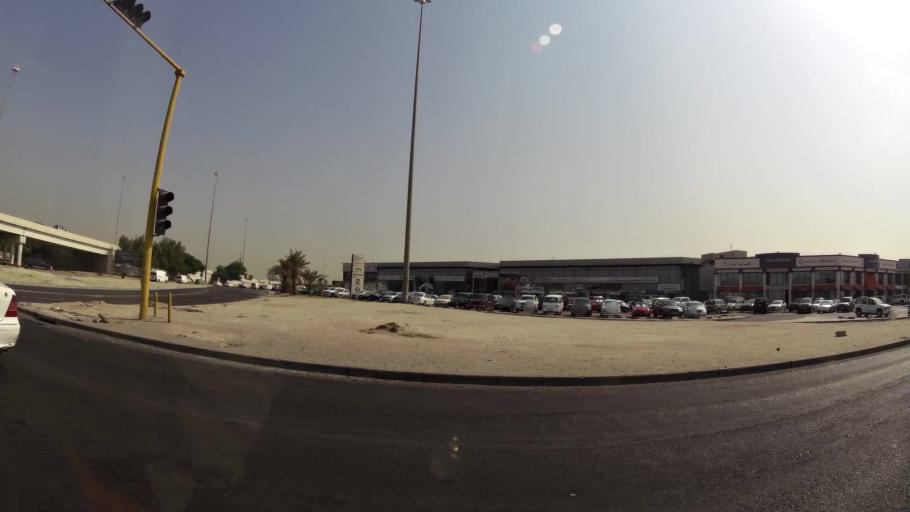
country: KW
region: Al Asimah
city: Ar Rabiyah
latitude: 29.3124
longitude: 47.9264
